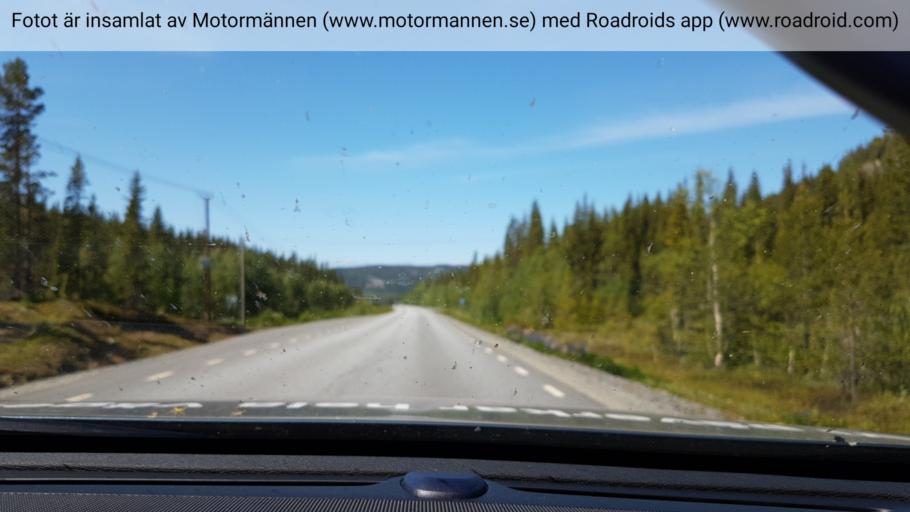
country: SE
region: Vaesterbotten
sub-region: Vilhelmina Kommun
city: Sjoberg
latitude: 64.7105
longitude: 15.4371
